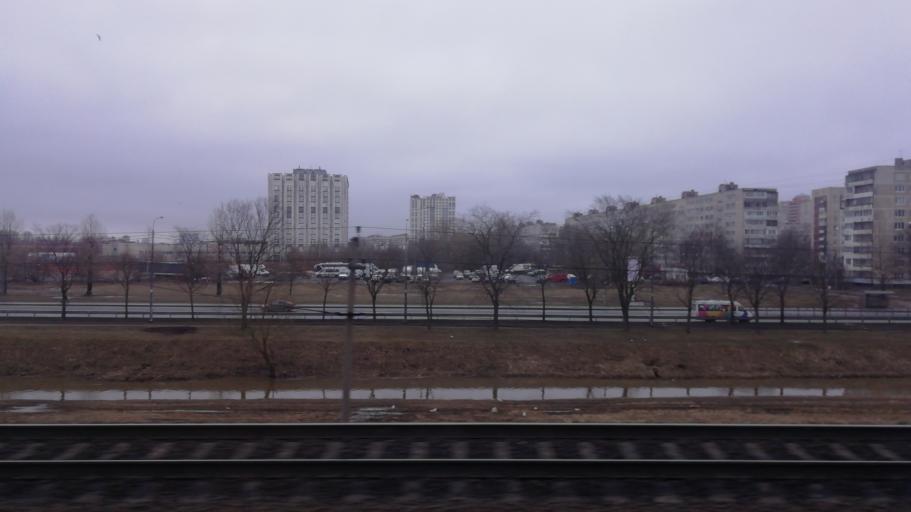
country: RU
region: St.-Petersburg
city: Kupchino
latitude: 59.8723
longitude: 30.3553
